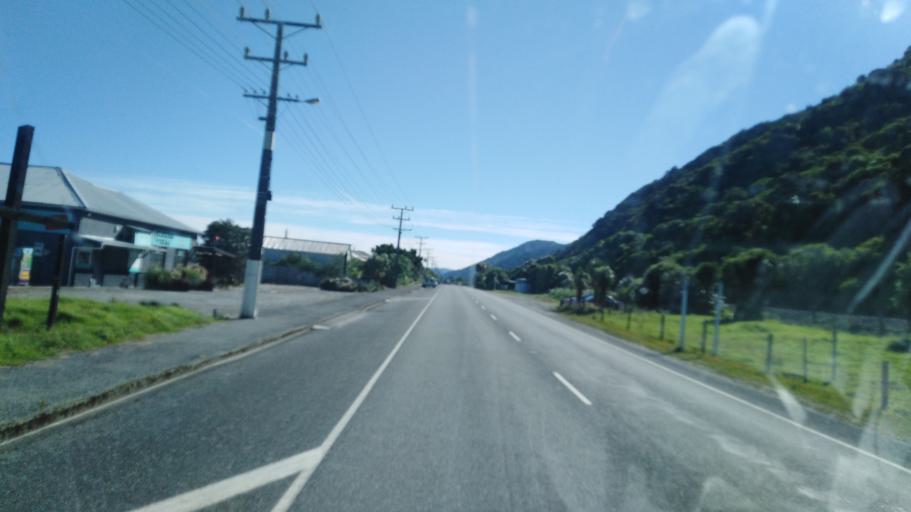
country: NZ
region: West Coast
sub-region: Buller District
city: Westport
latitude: -41.6264
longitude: 171.8567
